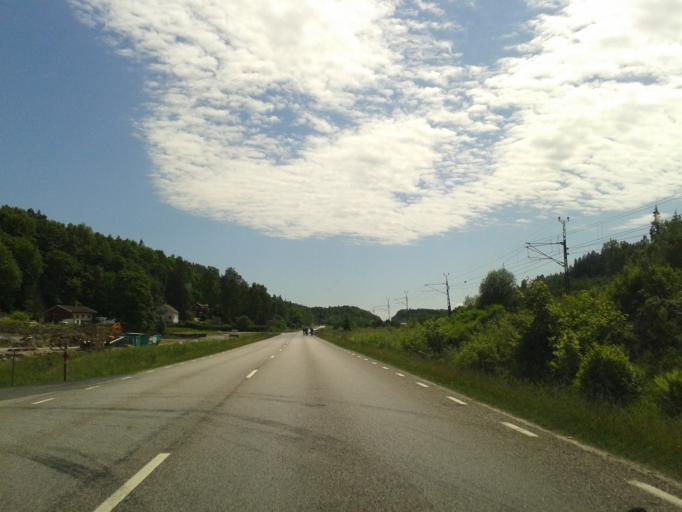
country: SE
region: Vaestra Goetaland
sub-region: Uddevalla Kommun
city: Ljungskile
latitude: 58.2728
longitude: 11.8903
